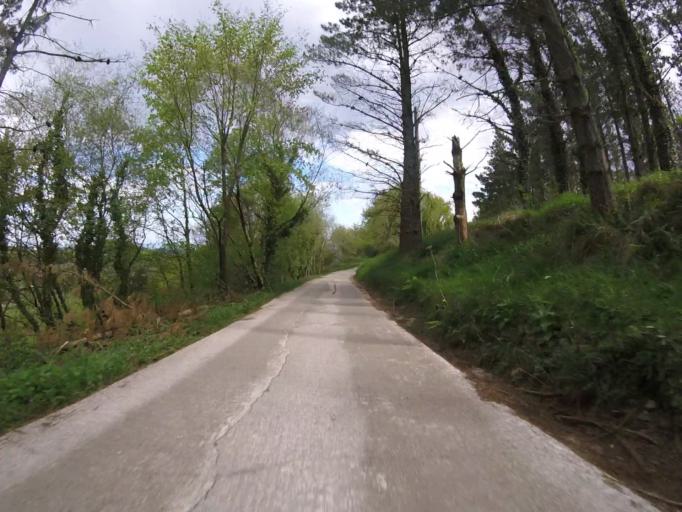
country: ES
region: Basque Country
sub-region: Provincia de Guipuzcoa
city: Zarautz
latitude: 43.2510
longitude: -2.1833
